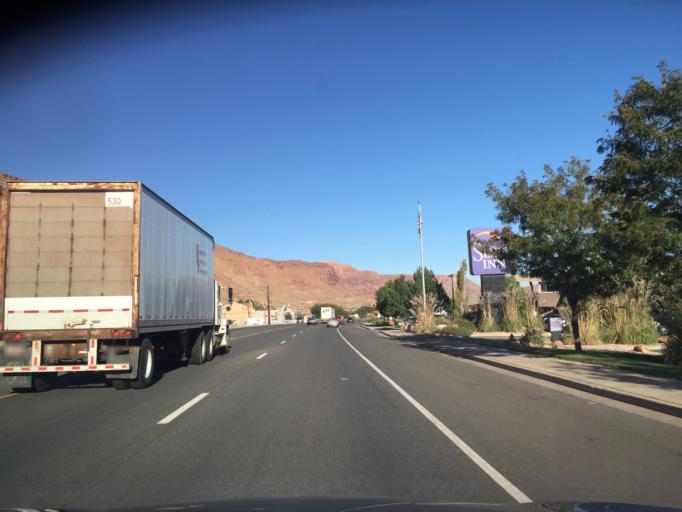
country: US
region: Utah
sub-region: Grand County
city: Moab
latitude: 38.5567
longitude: -109.5405
